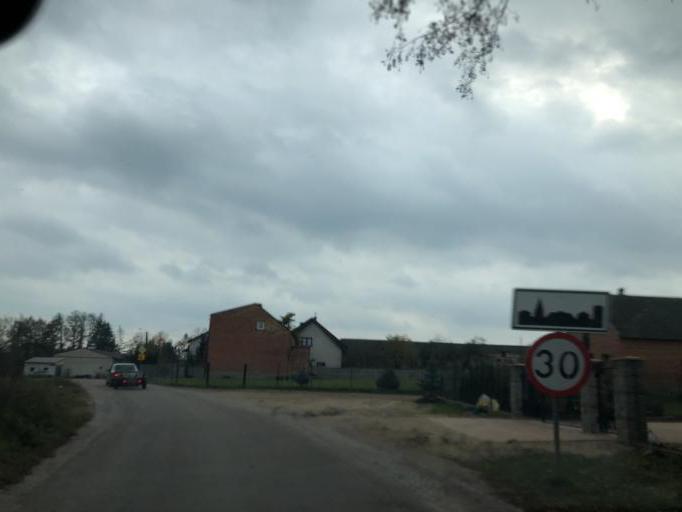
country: PL
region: Podlasie
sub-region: Lomza
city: Lomza
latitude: 53.1597
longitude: 22.0010
